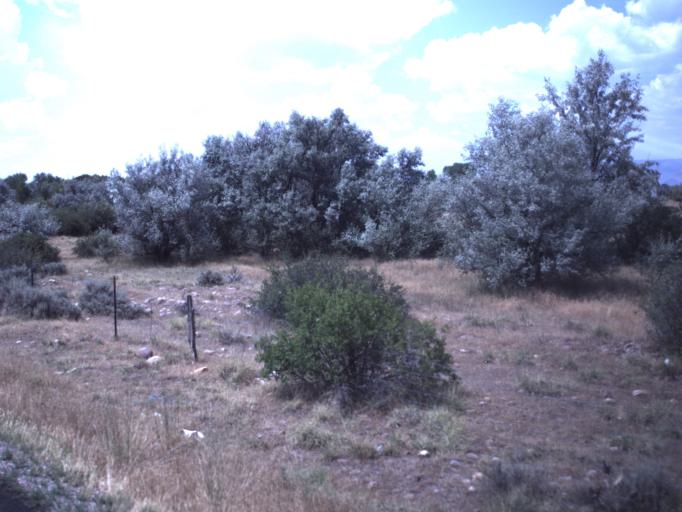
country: US
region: Utah
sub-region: Duchesne County
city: Roosevelt
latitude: 40.4038
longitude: -109.8689
